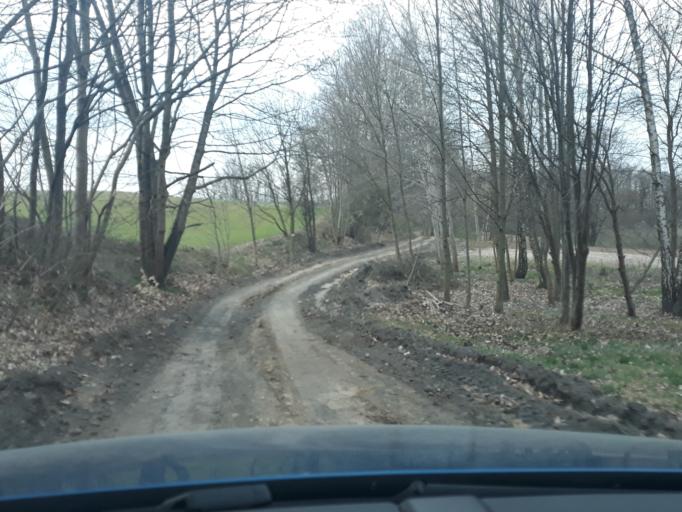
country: PL
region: Pomeranian Voivodeship
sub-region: Powiat chojnicki
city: Chojnice
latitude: 53.7247
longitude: 17.4901
